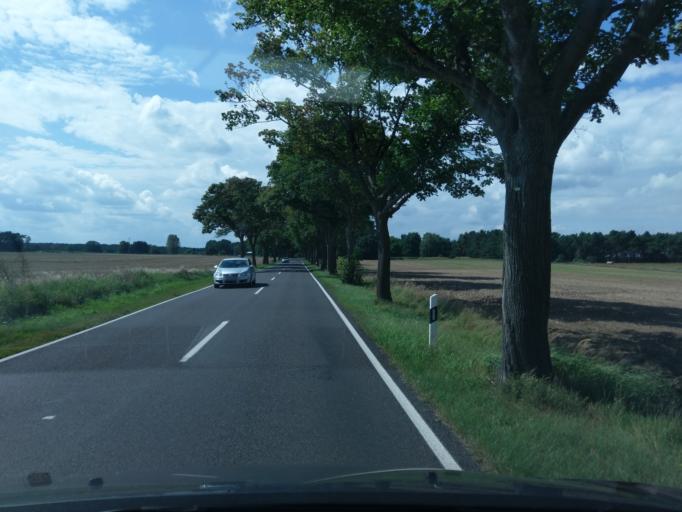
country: DE
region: Brandenburg
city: Borkwalde
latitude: 52.3022
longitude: 12.7905
